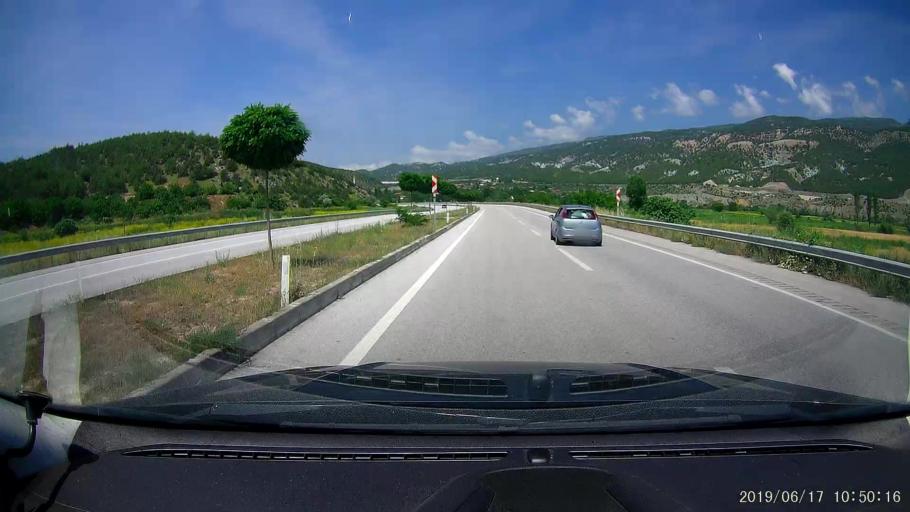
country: TR
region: Corum
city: Hacihamza
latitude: 41.0982
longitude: 34.3893
